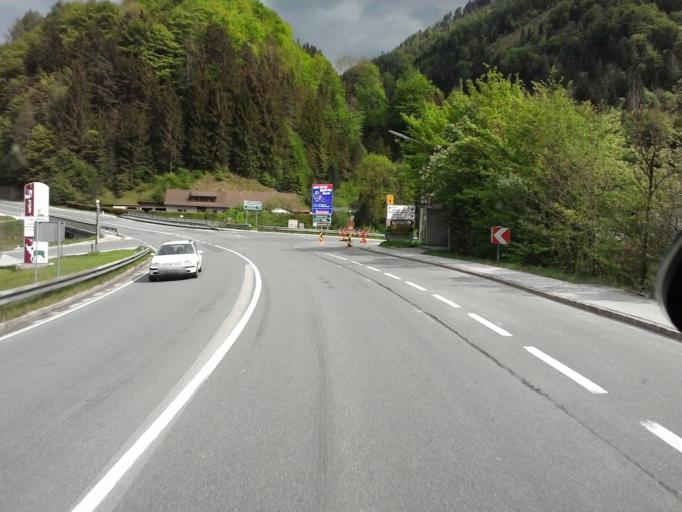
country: AT
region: Upper Austria
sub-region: Politischer Bezirk Kirchdorf an der Krems
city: Micheldorf in Oberoesterreich
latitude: 47.7716
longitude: 14.1698
